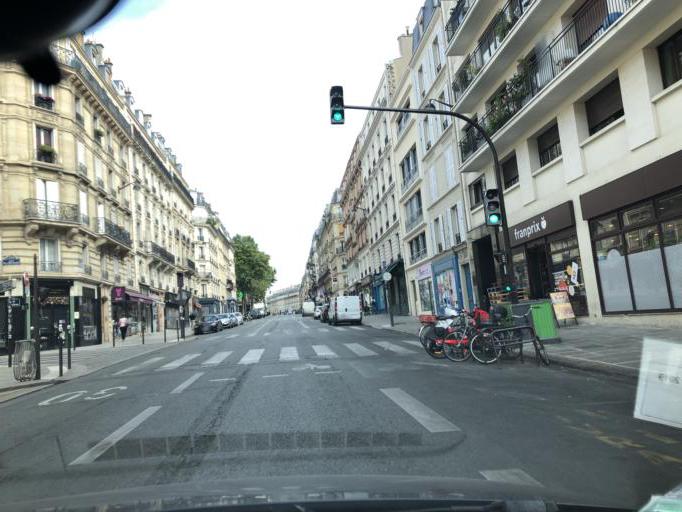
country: FR
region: Ile-de-France
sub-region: Paris
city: Paris
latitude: 48.8414
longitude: 2.3520
